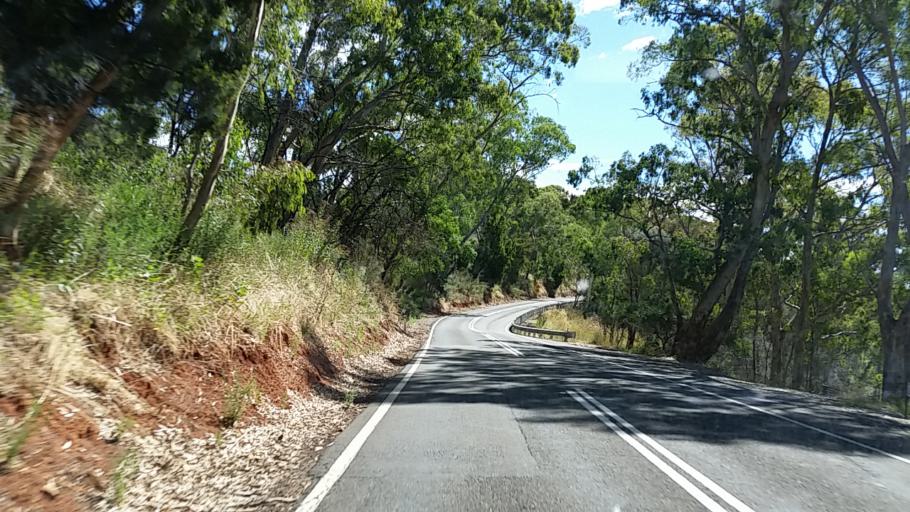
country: AU
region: South Australia
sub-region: Adelaide Hills
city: Gumeracha
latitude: -34.8434
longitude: 138.8377
